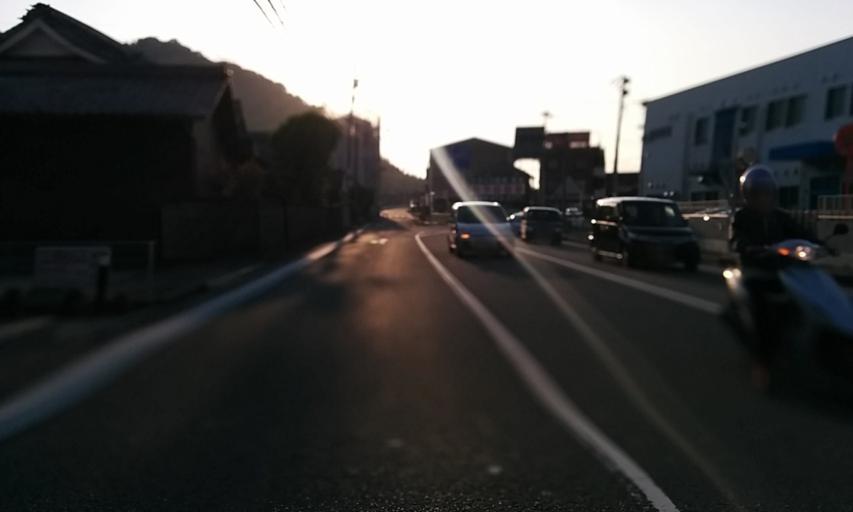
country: JP
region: Ehime
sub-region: Shikoku-chuo Shi
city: Matsuyama
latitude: 33.7821
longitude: 132.7870
